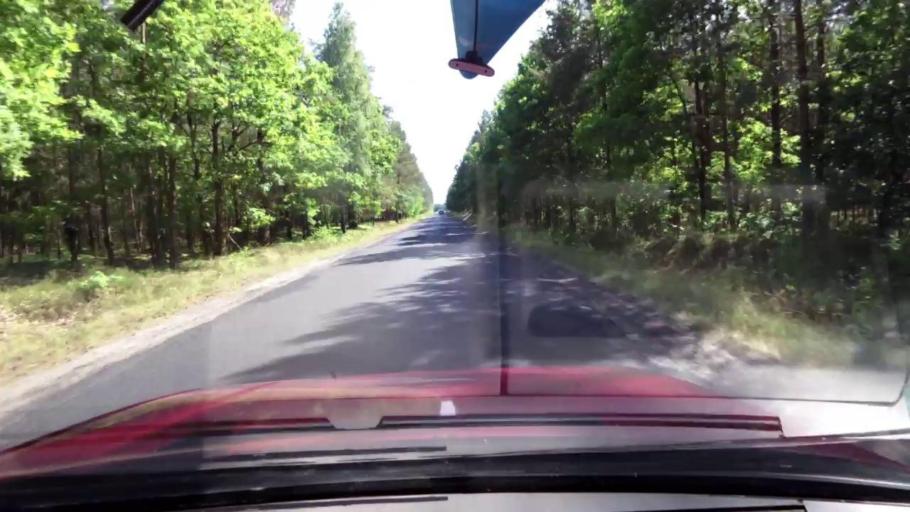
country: PL
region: Pomeranian Voivodeship
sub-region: Powiat slupski
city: Kepice
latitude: 54.3032
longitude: 16.9616
